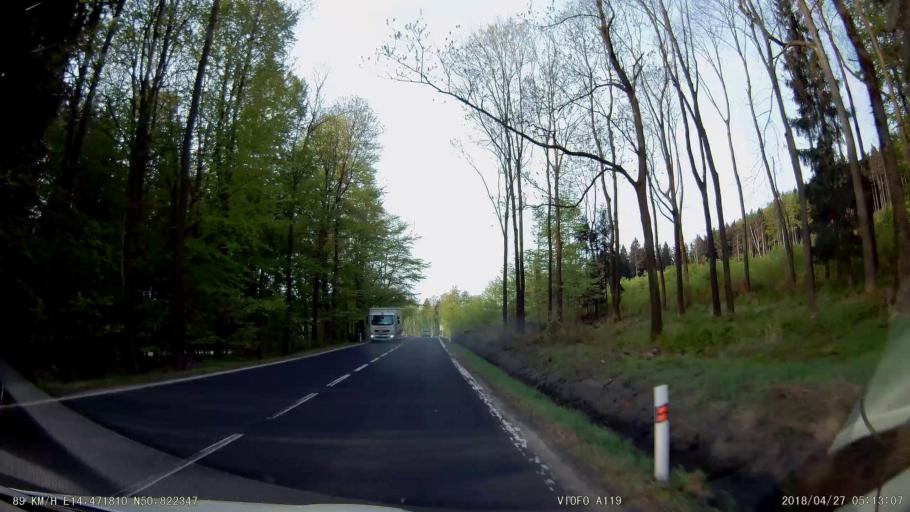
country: CZ
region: Ustecky
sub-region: Okres Decin
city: Chribska
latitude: 50.8221
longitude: 14.4718
